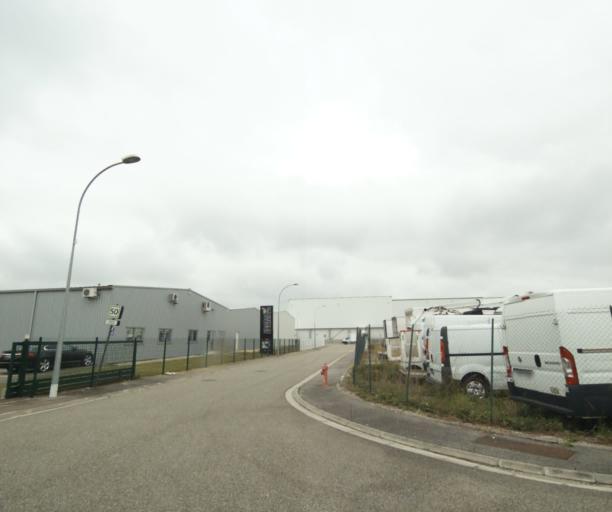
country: FR
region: Midi-Pyrenees
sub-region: Departement du Tarn-et-Garonne
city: Bressols
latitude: 43.9794
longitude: 1.3264
